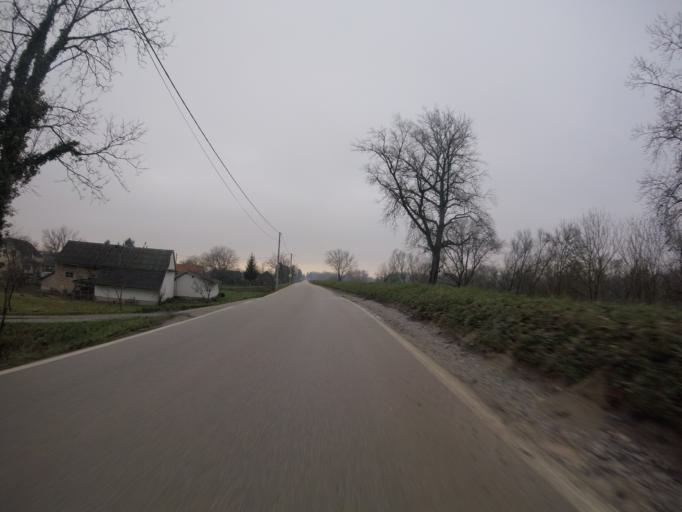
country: HR
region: Zagrebacka
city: Kuce
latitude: 45.6920
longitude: 16.2299
